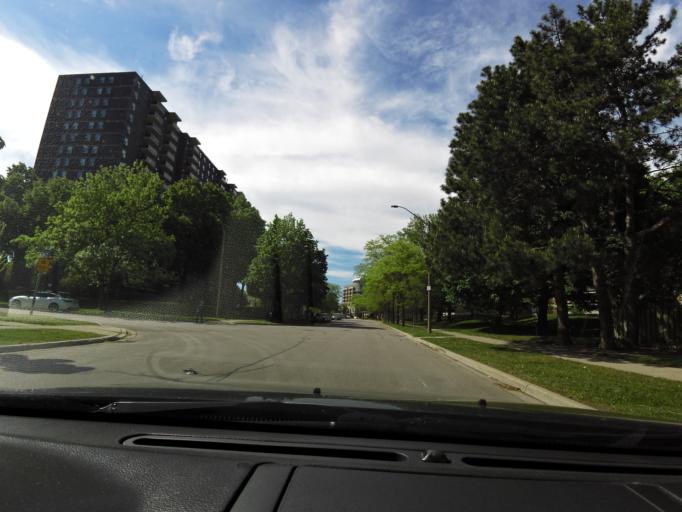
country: CA
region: Ontario
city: Mississauga
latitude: 43.5118
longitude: -79.6255
